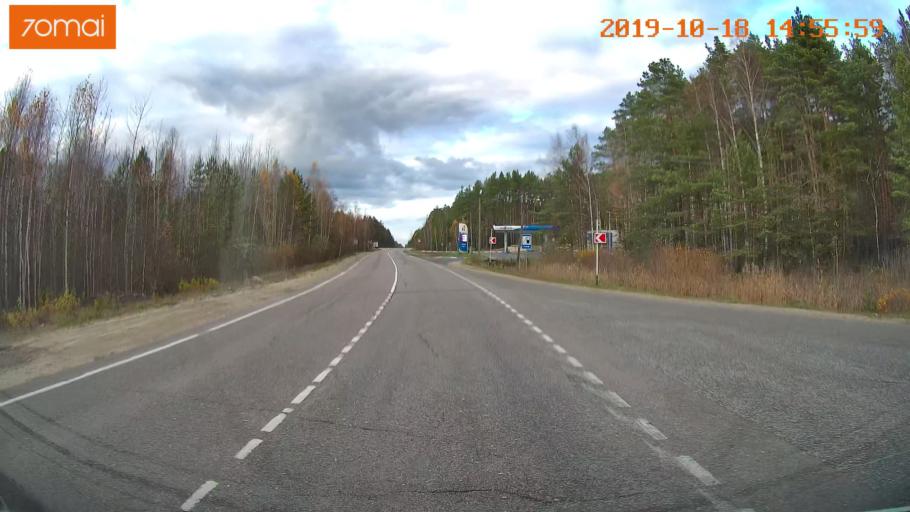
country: RU
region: Vladimir
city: Kurlovo
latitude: 55.4590
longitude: 40.5896
